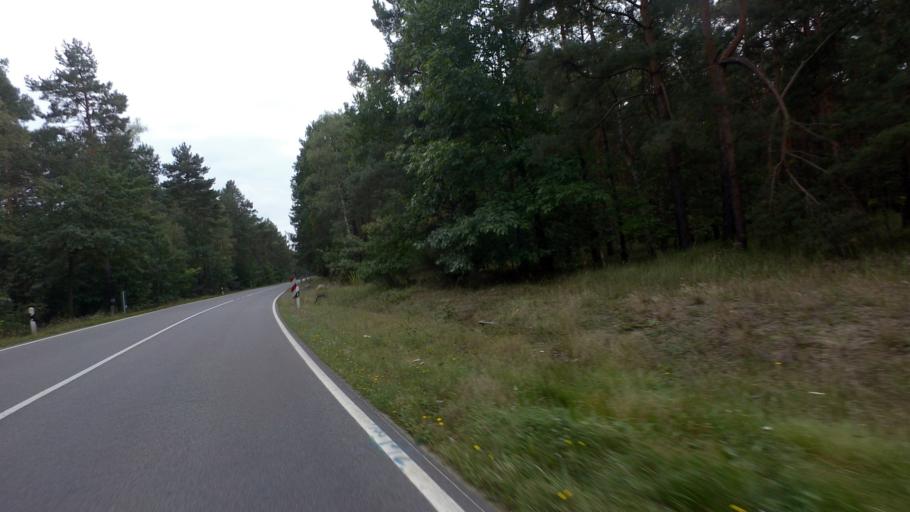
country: DE
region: Saxony
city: Wittichenau
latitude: 51.3806
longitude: 14.2973
